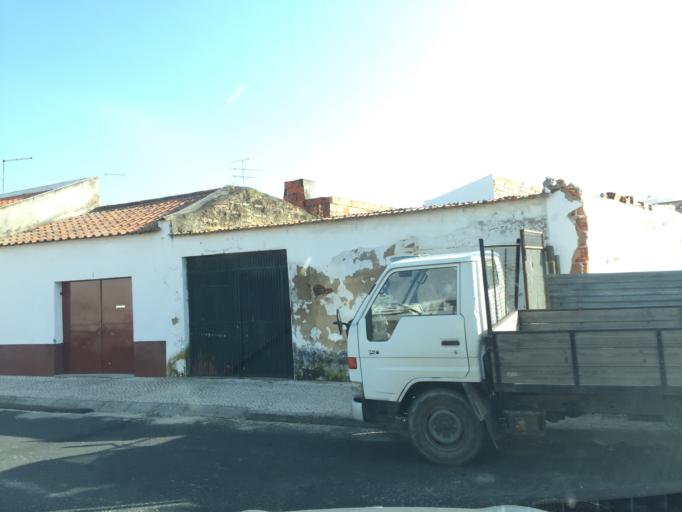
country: PT
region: Santarem
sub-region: Almeirim
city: Almeirim
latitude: 39.2125
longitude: -8.6260
